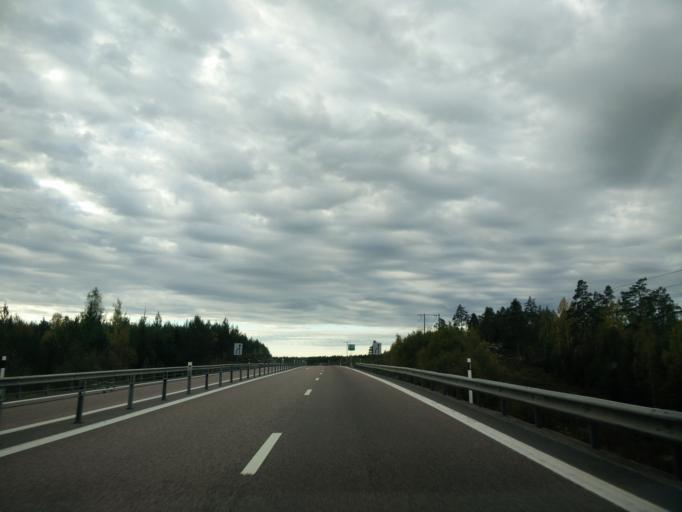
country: SE
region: Gaevleborg
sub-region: Hudiksvalls Kommun
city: Hudiksvall
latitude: 61.7338
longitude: 17.0671
